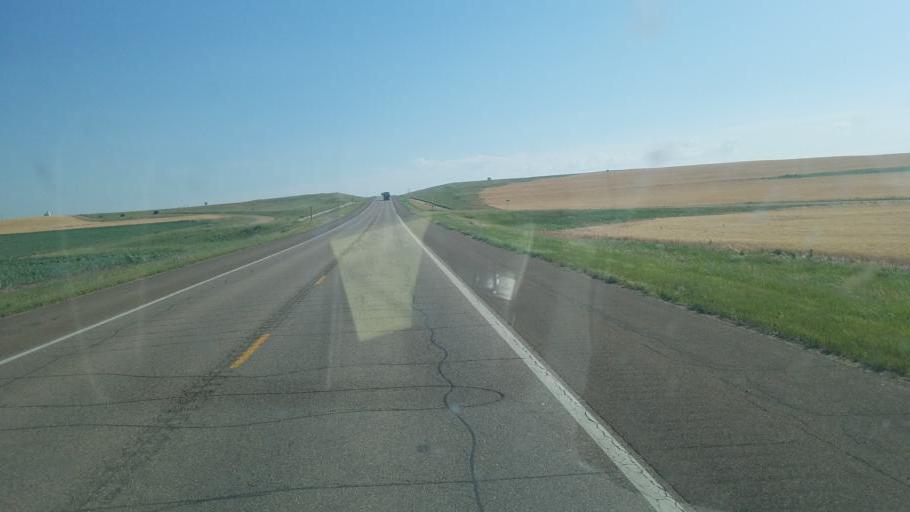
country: US
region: Kansas
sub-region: Barton County
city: Great Bend
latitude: 38.3811
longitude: -98.6838
